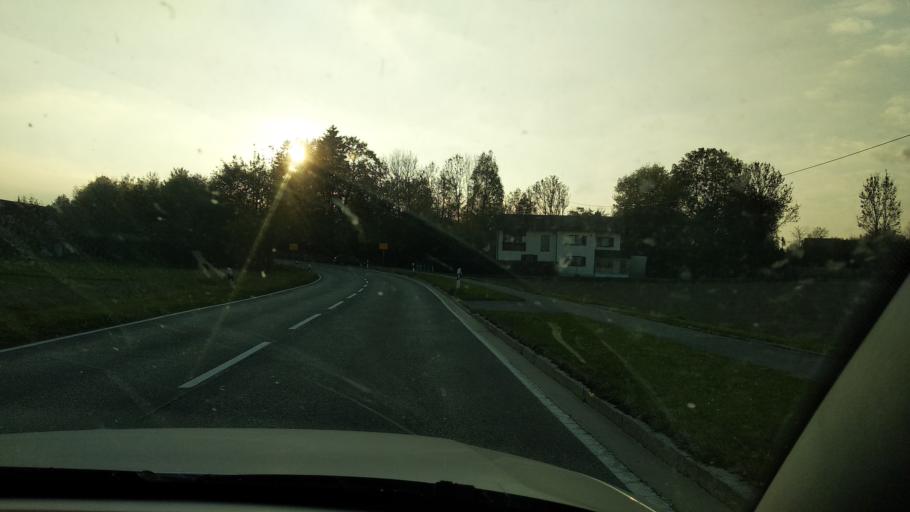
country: DE
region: Bavaria
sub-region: Upper Bavaria
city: Markt Schwaben
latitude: 48.1969
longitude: 11.8780
